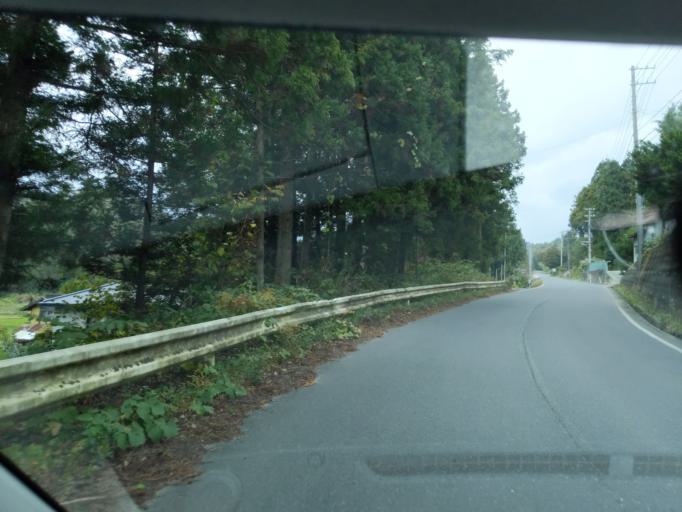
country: JP
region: Iwate
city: Mizusawa
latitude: 39.0469
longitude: 141.1149
